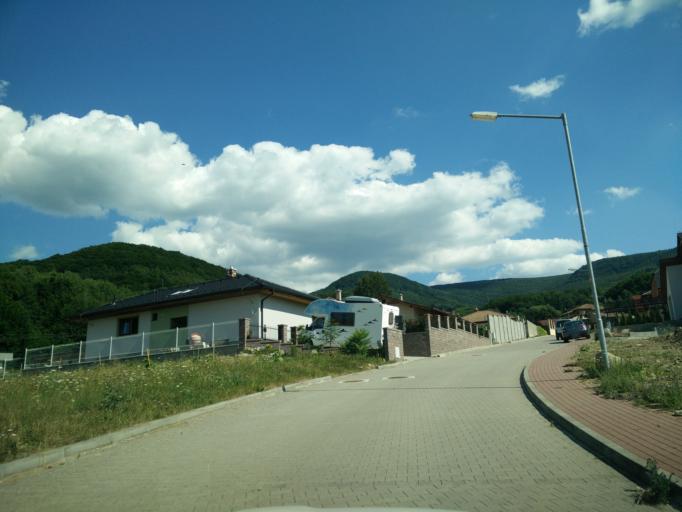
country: SK
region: Nitriansky
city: Prievidza
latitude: 48.7096
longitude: 18.6504
